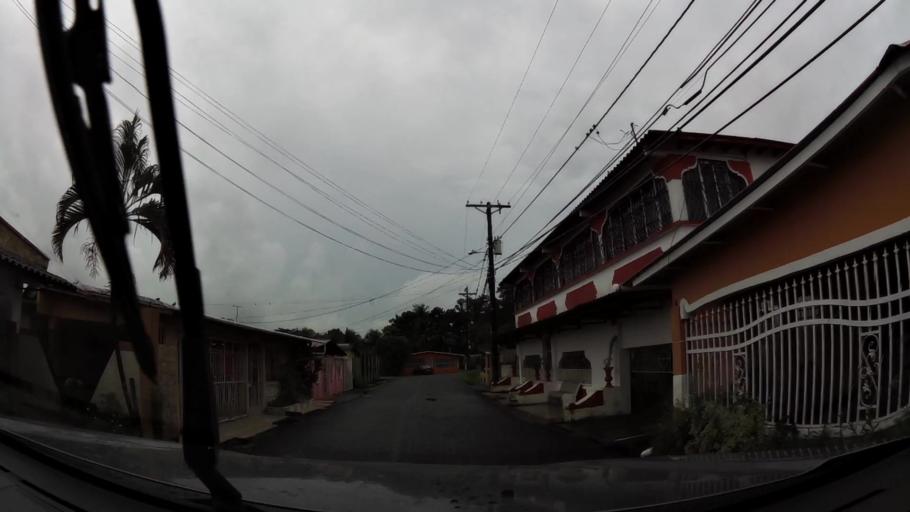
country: PA
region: Colon
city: Arco Iris
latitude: 9.3378
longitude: -79.8763
